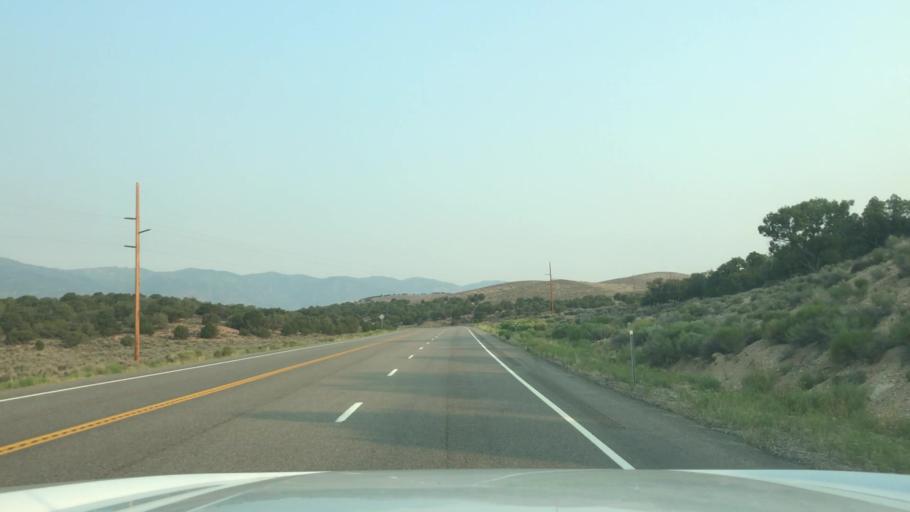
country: US
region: Utah
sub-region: Sevier County
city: Aurora
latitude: 38.9925
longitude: -112.0079
